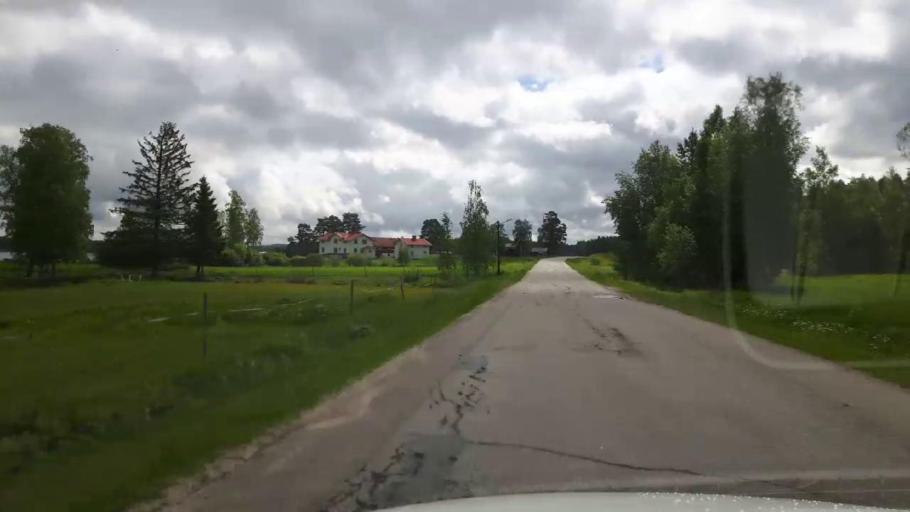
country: SE
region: Gaevleborg
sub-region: Ovanakers Kommun
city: Edsbyn
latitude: 61.3481
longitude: 15.9226
